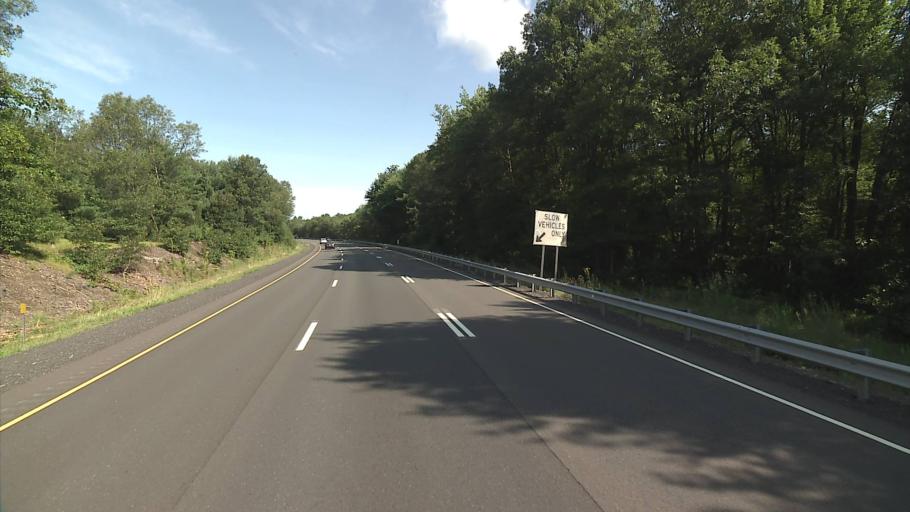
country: US
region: Connecticut
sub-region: Hartford County
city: Glastonbury Center
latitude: 41.6905
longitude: -72.5397
